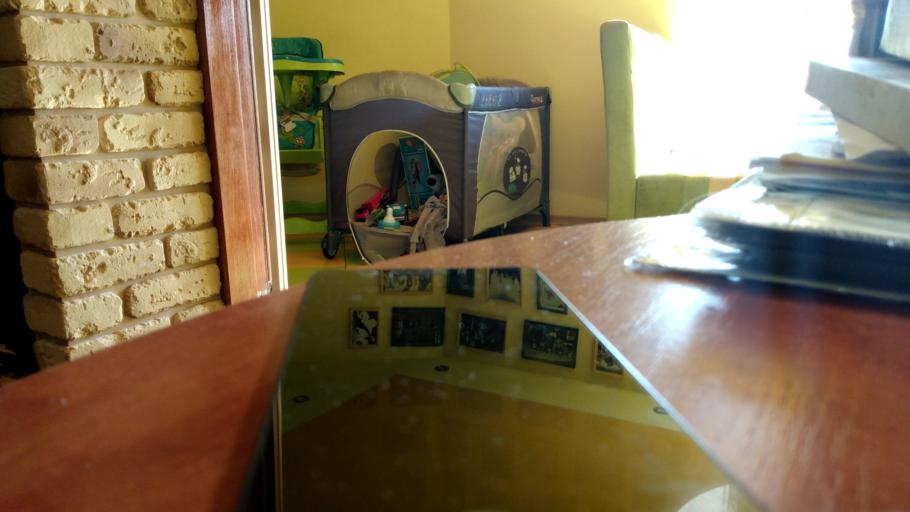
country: RU
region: Penza
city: Serdobsk
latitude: 52.3018
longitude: 44.3968
